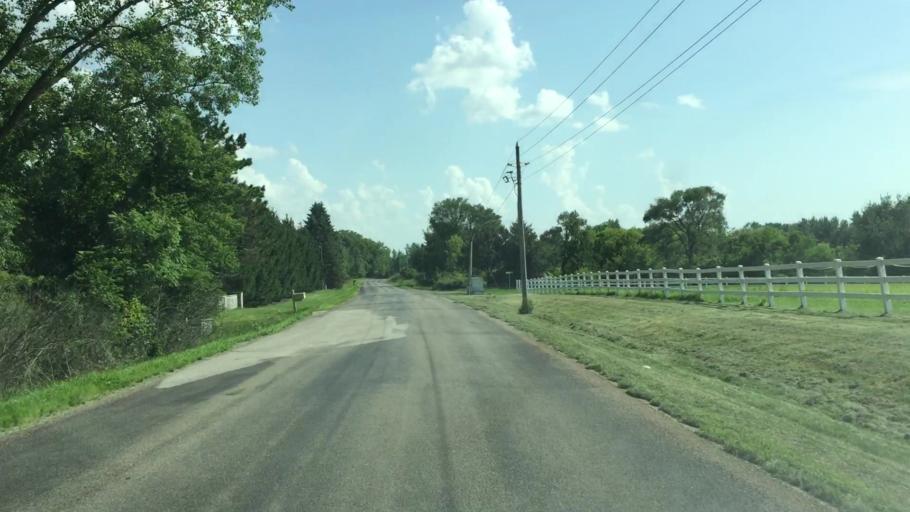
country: US
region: Iowa
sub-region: Johnson County
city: North Liberty
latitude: 41.8087
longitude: -91.6154
